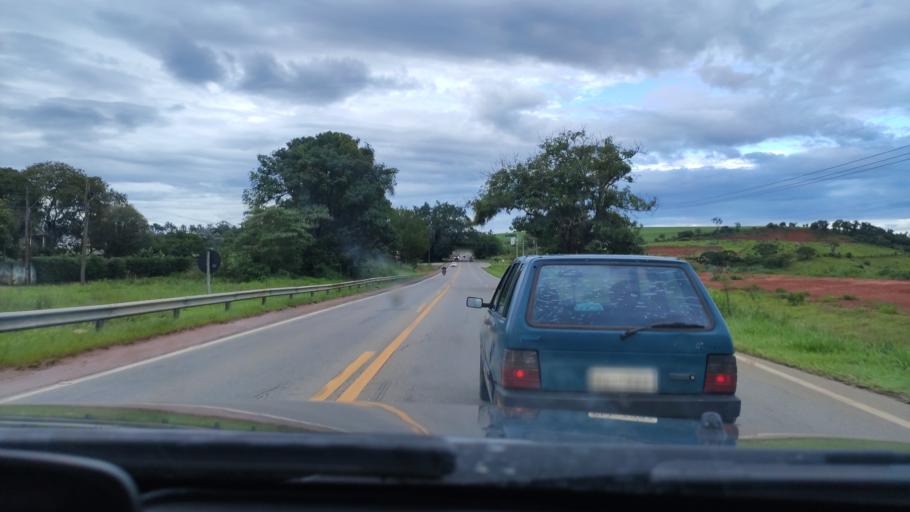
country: BR
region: Sao Paulo
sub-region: Braganca Paulista
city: Braganca Paulista
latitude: -22.8925
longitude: -46.5421
